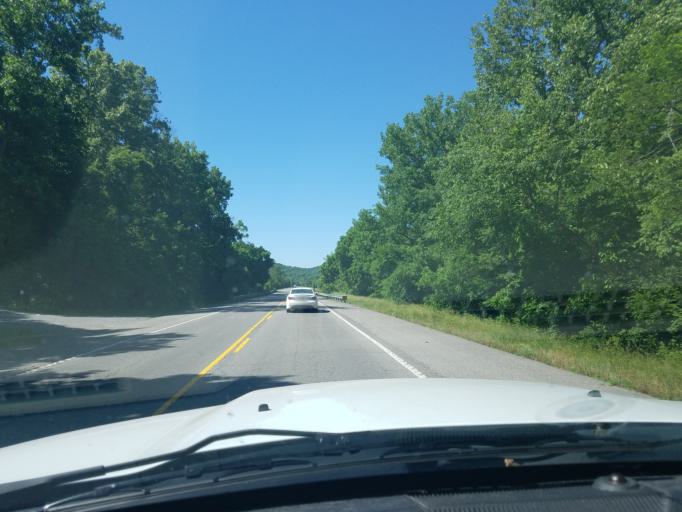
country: US
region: Tennessee
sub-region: Sumner County
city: Westmoreland
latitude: 36.5188
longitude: -86.2625
